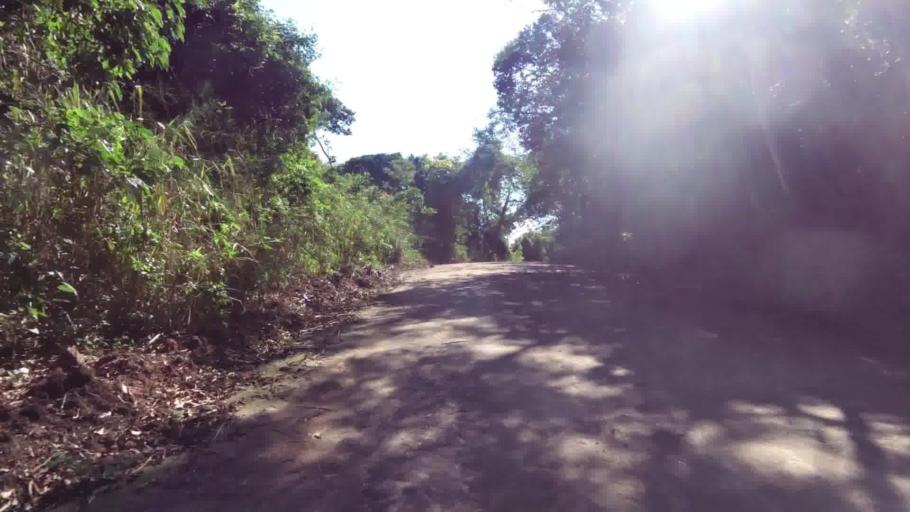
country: BR
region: Espirito Santo
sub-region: Piuma
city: Piuma
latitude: -20.8233
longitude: -40.6175
